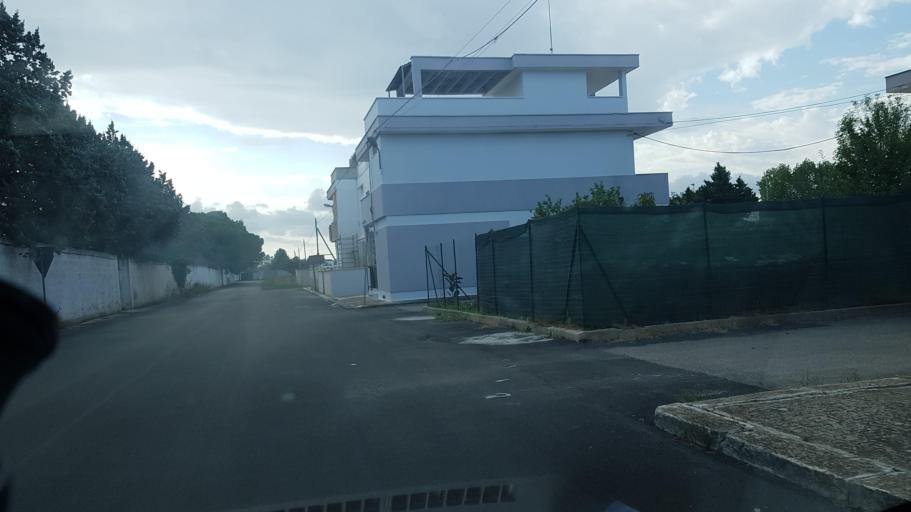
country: IT
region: Apulia
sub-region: Provincia di Brindisi
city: San Pietro Vernotico
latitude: 40.4868
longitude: 18.0047
